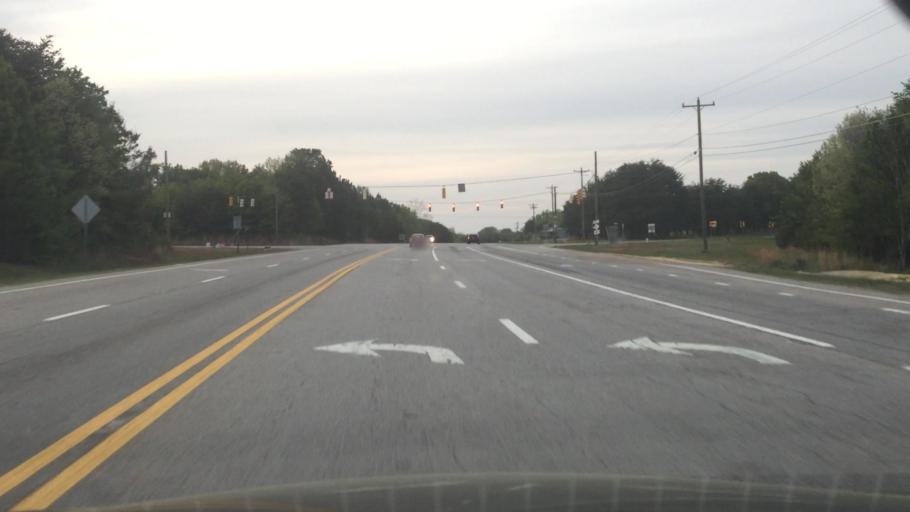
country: US
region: North Carolina
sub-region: Rockingham County
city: Reidsville
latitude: 36.3126
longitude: -79.6300
